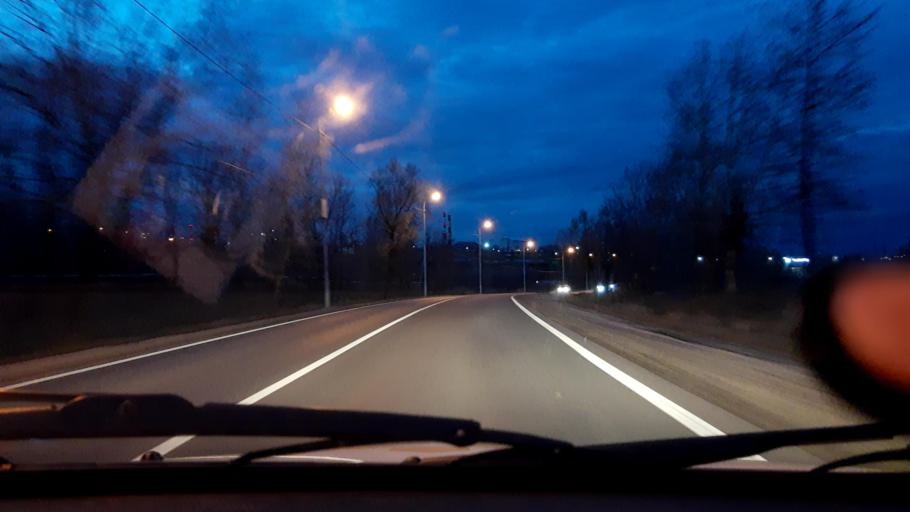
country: RU
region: Bashkortostan
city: Ufa
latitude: 54.8676
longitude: 56.1012
